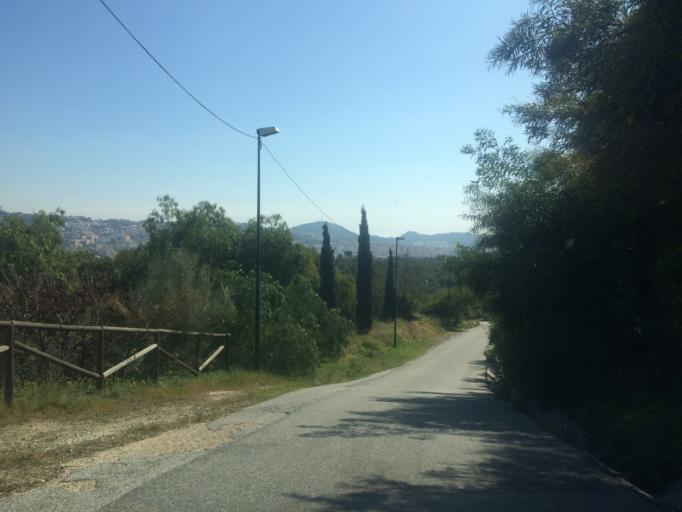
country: ES
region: Andalusia
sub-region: Provincia de Malaga
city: Malaga
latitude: 36.7523
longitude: -4.4356
